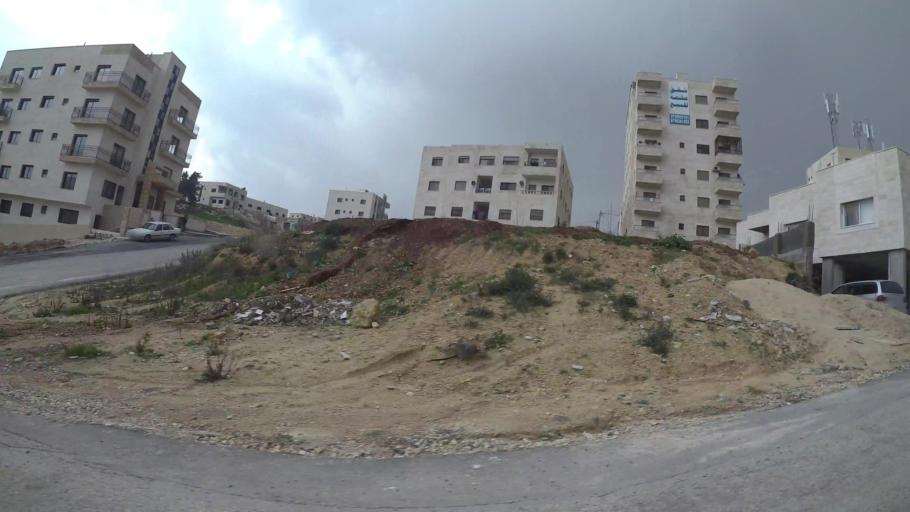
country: JO
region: Amman
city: Umm as Summaq
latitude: 31.8824
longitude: 35.8545
